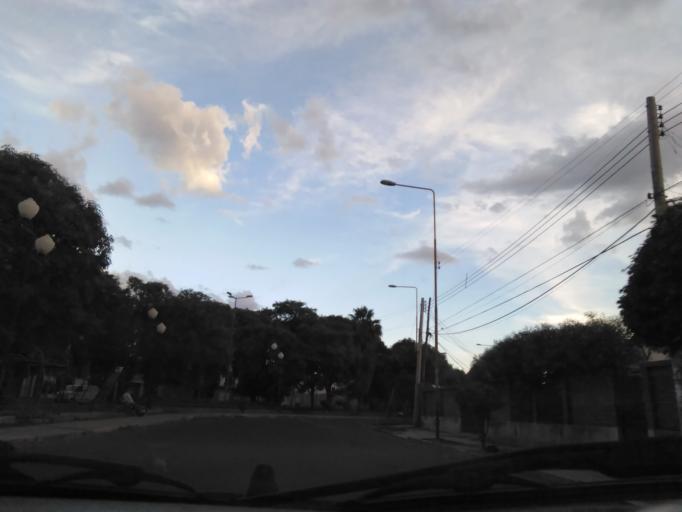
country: BO
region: Cochabamba
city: Cochabamba
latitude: -17.3858
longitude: -66.1696
